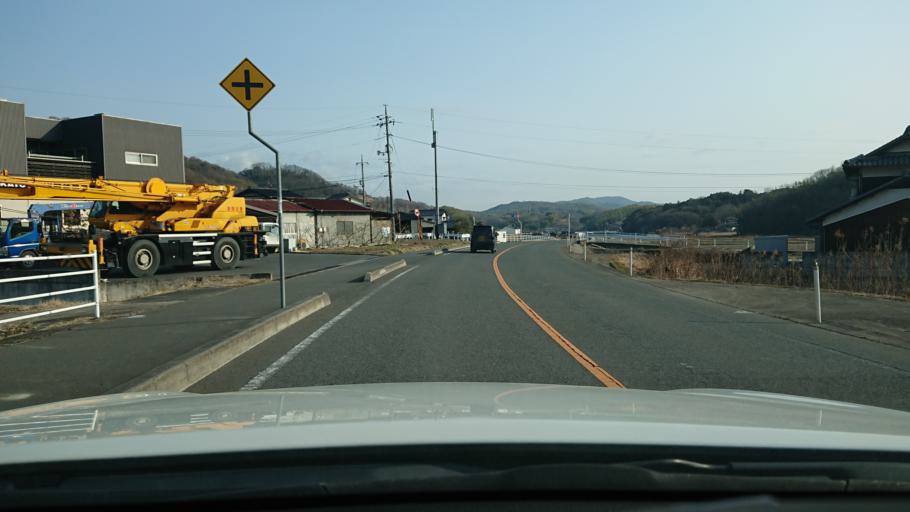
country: JP
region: Okayama
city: Kurashiki
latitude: 34.6013
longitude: 133.7011
